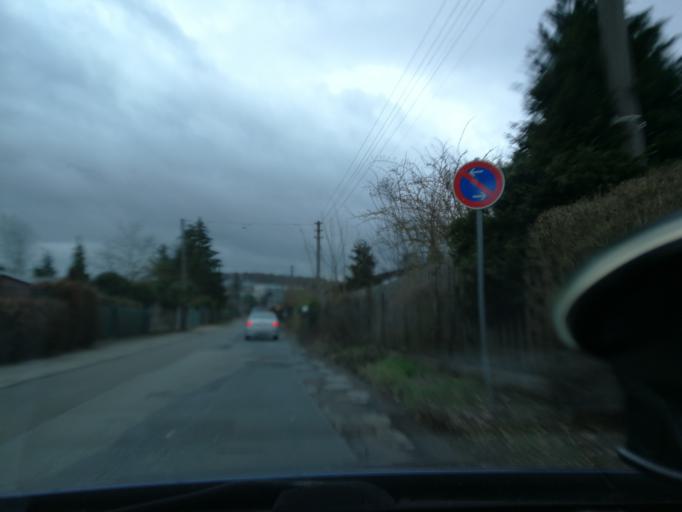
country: DE
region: Rheinland-Pfalz
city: Trier
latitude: 49.7289
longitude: 6.6391
